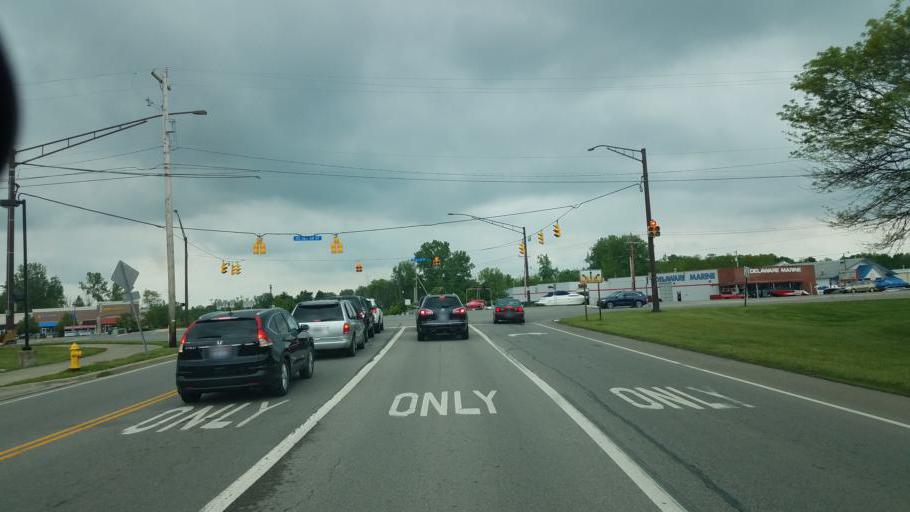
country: US
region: Ohio
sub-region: Delaware County
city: Delaware
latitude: 40.2958
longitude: -83.0381
